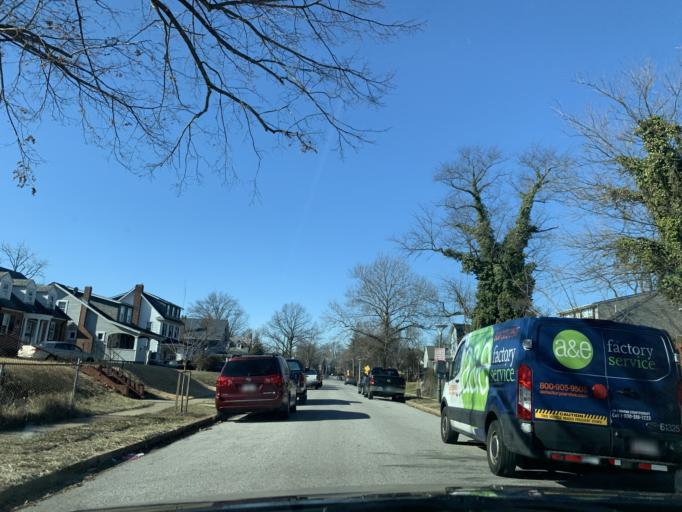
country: US
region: Maryland
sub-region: Baltimore County
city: Lochearn
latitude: 39.3305
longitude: -76.6855
